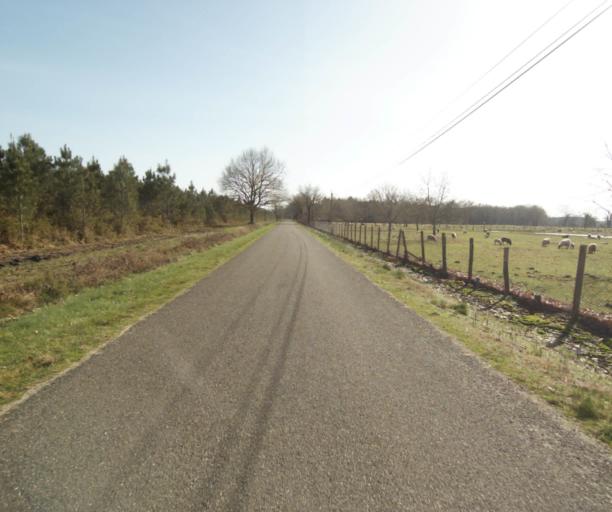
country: FR
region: Aquitaine
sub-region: Departement des Landes
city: Roquefort
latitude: 44.1370
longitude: -0.2597
